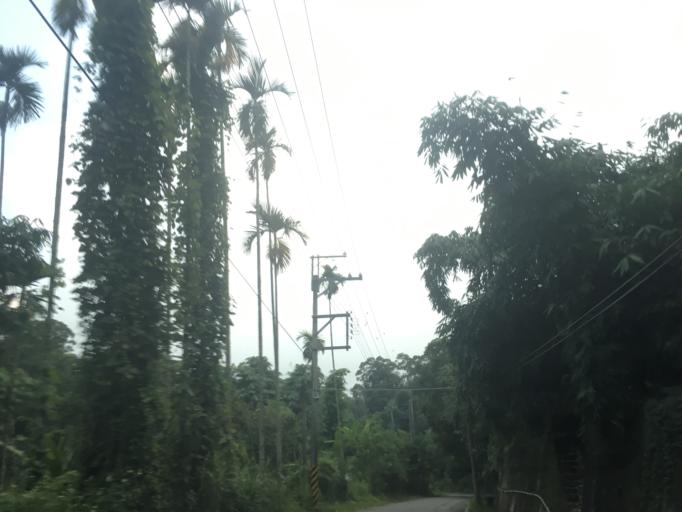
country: TW
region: Taiwan
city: Fengyuan
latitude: 24.1913
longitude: 120.7771
